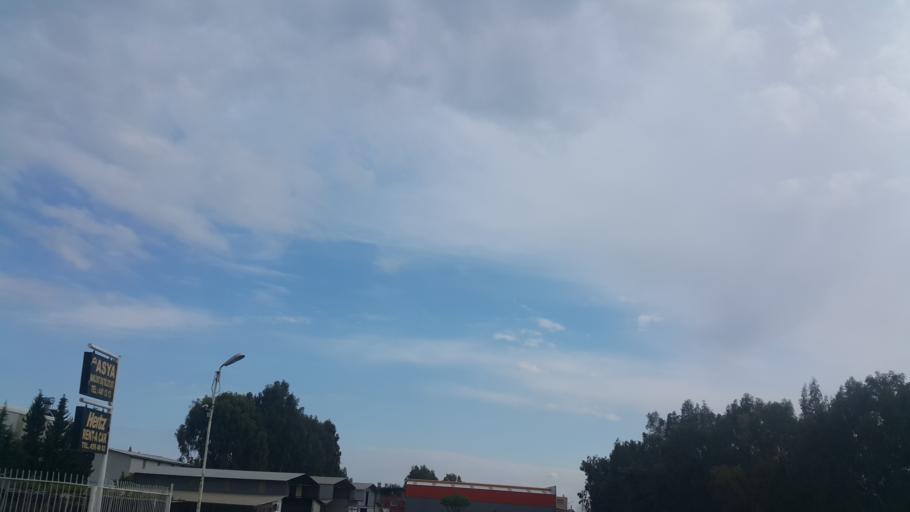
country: TR
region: Adana
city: Seyhan
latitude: 36.9944
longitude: 35.2105
